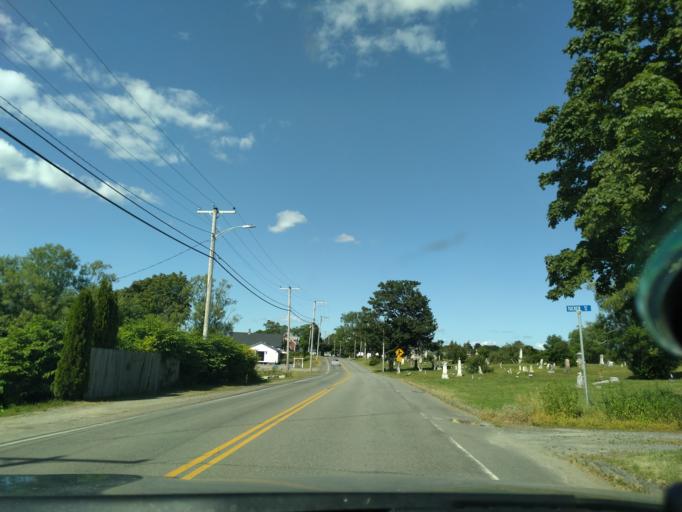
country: US
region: Maine
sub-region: Washington County
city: Eastport
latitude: 44.8545
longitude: -66.9935
